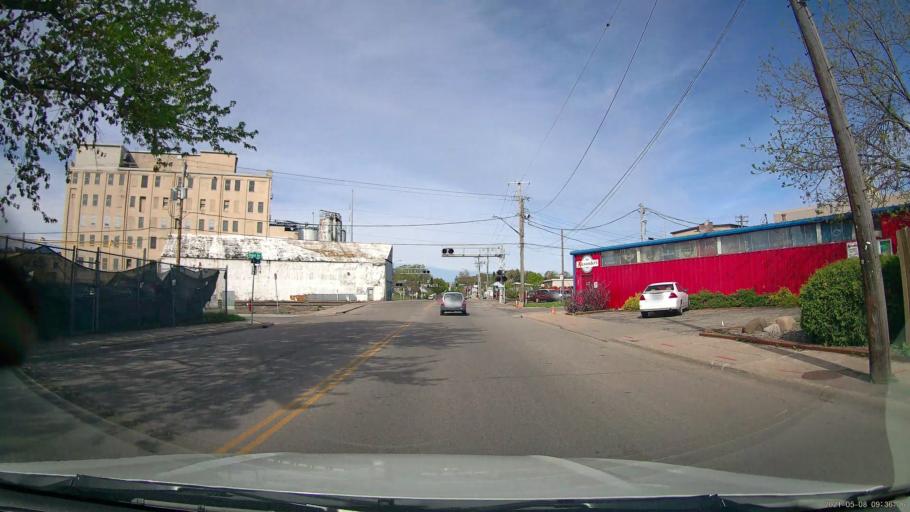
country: US
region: Minnesota
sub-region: Hennepin County
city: Minneapolis
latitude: 44.9396
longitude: -93.2302
